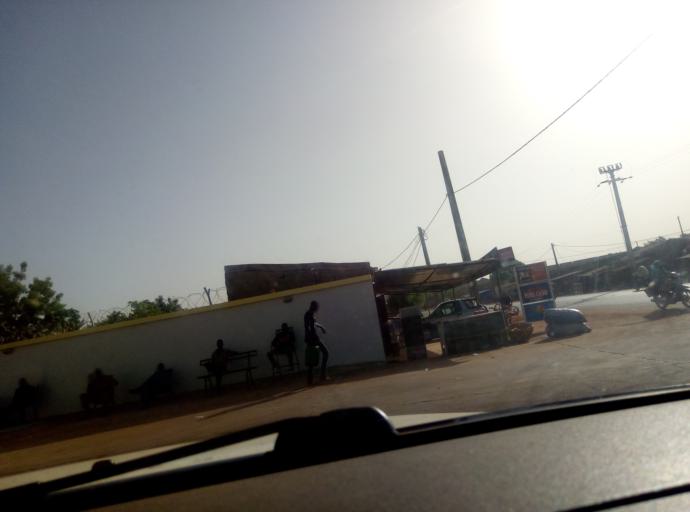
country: ML
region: Bamako
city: Bamako
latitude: 12.5864
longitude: -7.7676
